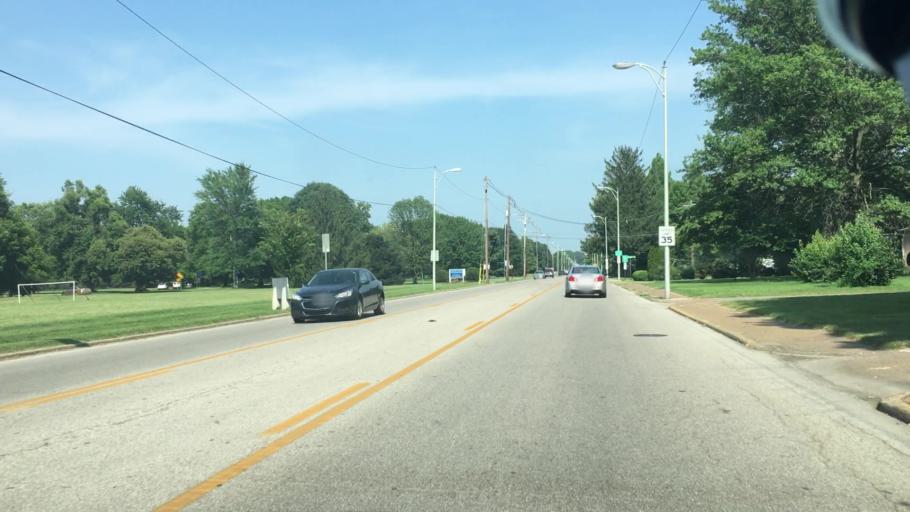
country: US
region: Indiana
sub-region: Vanderburgh County
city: Evansville
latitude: 37.9698
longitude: -87.5100
